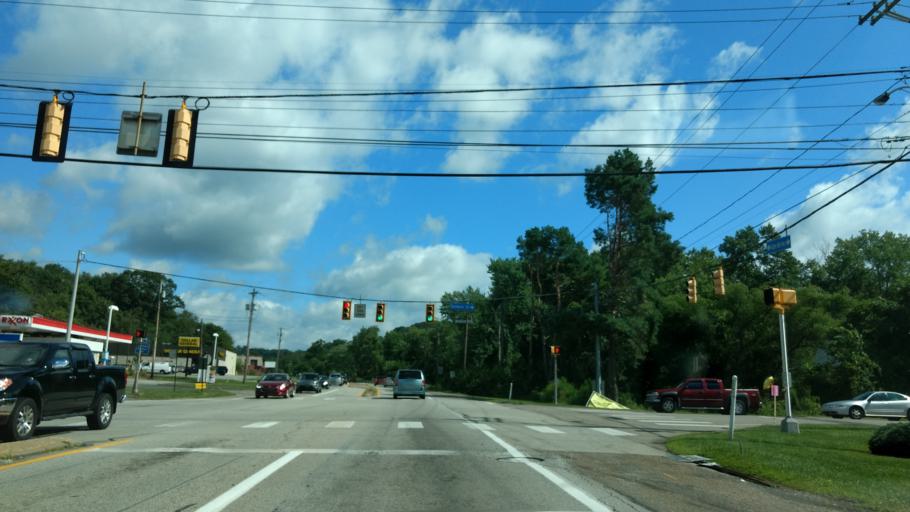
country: US
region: Pennsylvania
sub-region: Westmoreland County
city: Murrysville
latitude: 40.4633
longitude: -79.7055
